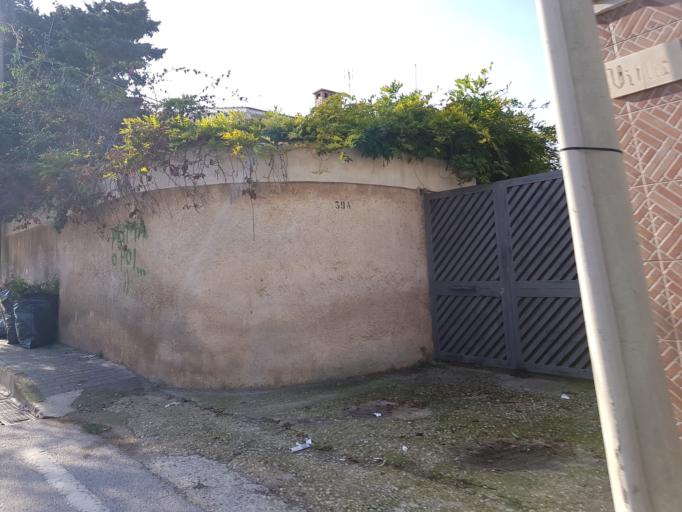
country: IT
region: Apulia
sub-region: Provincia di Brindisi
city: Materdomini
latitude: 40.6557
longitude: 17.9564
